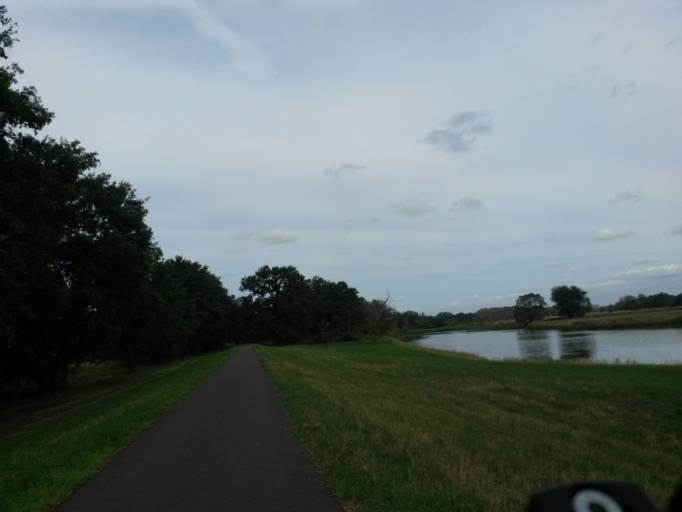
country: DE
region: Saxony-Anhalt
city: Tangermunde
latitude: 52.5109
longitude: 11.9560
